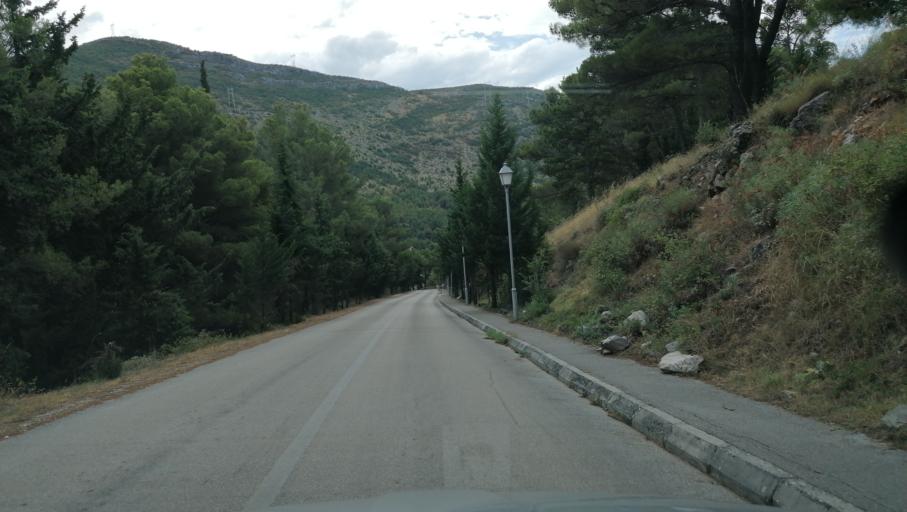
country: BA
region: Republika Srpska
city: Trebinje
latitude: 42.7107
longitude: 18.3618
